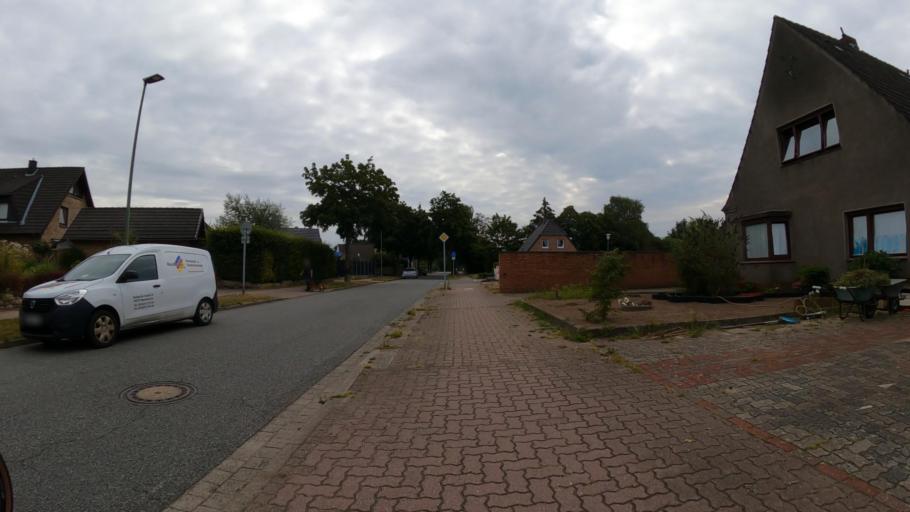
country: DE
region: Schleswig-Holstein
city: Boostedt
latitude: 54.0500
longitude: 10.0389
